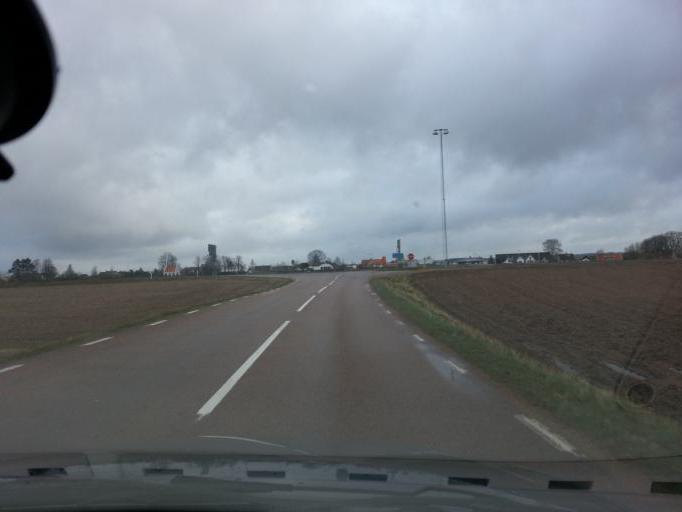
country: SE
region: Skane
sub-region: Astorps Kommun
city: Kvidinge
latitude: 56.1247
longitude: 13.0785
